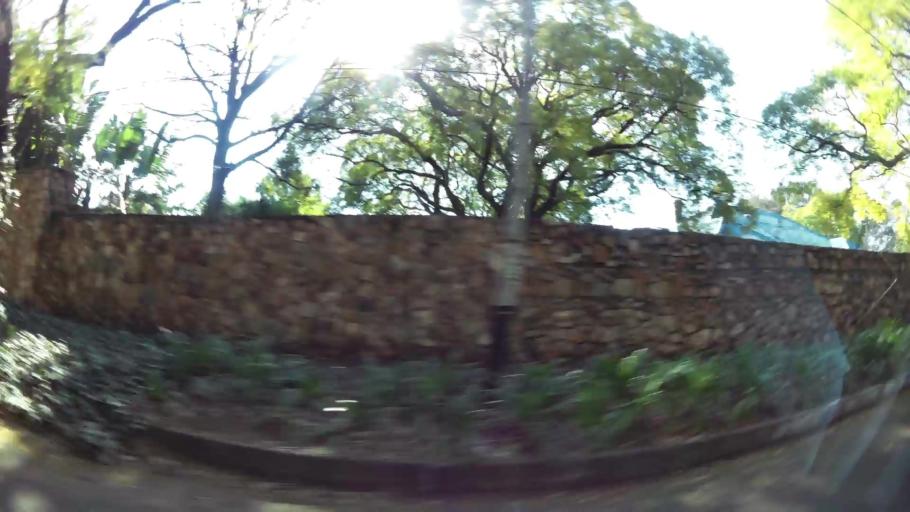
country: ZA
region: Gauteng
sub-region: City of Johannesburg Metropolitan Municipality
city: Johannesburg
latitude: -26.1712
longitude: 28.0769
